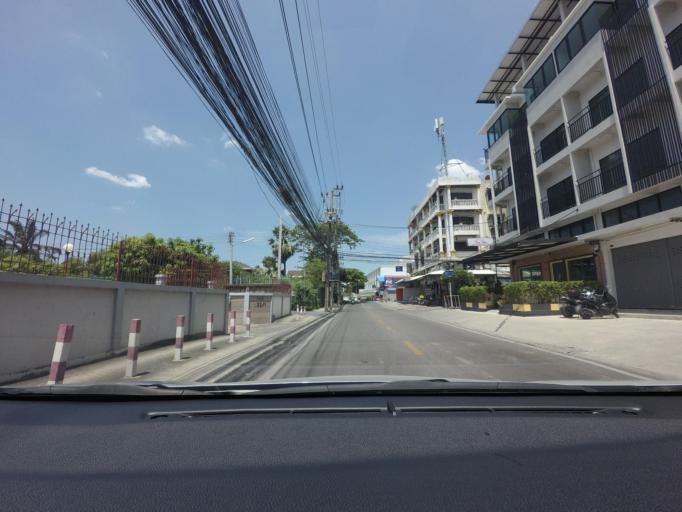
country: TH
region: Bangkok
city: Phra Khanong
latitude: 13.7207
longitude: 100.6138
